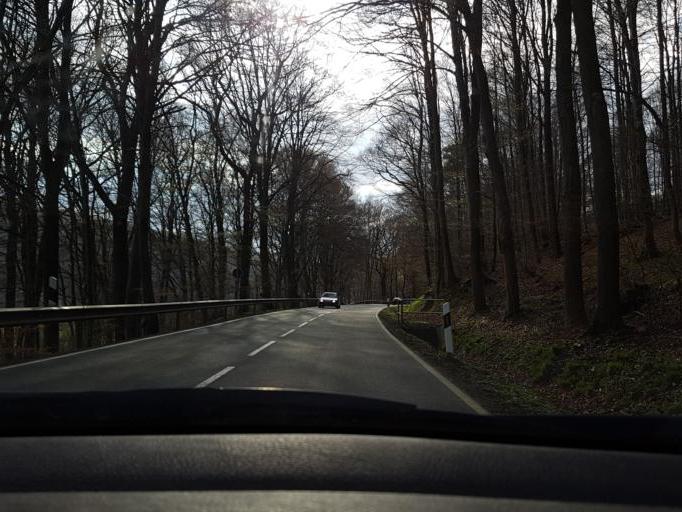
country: DE
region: Lower Saxony
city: Uslar
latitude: 51.6288
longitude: 9.6080
